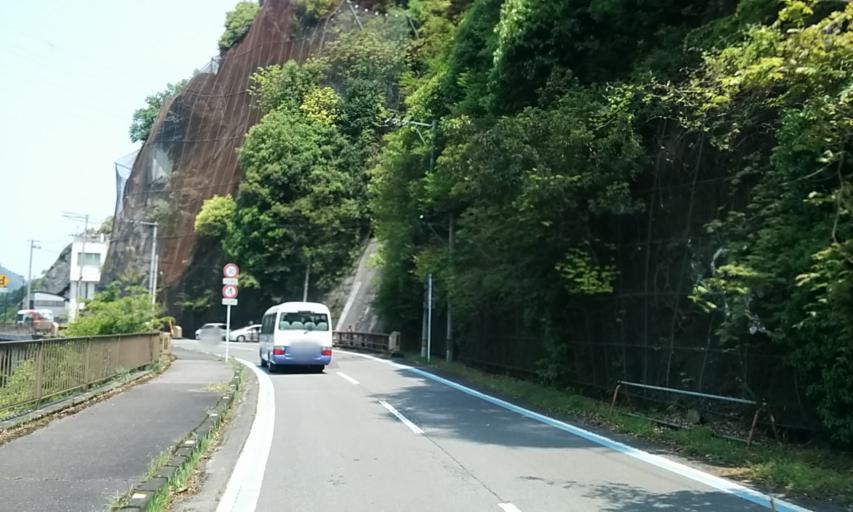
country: JP
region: Ehime
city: Niihama
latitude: 33.8929
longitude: 133.3105
